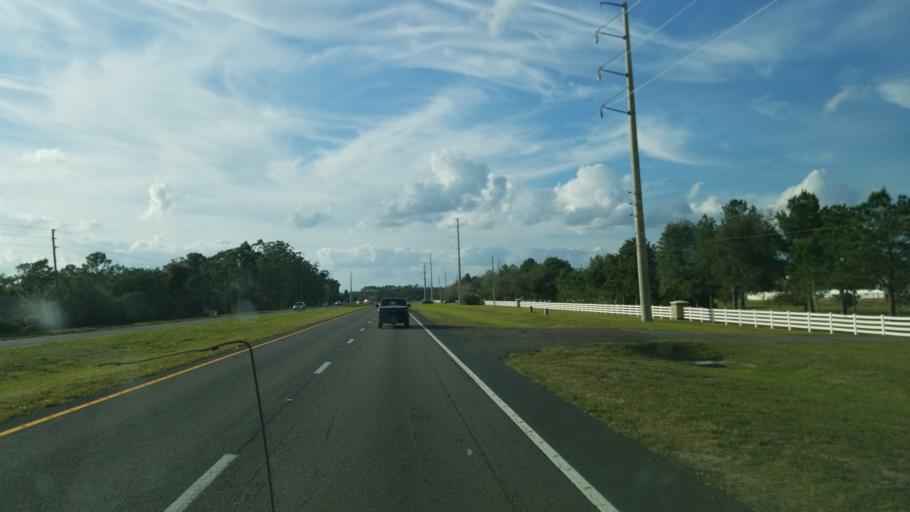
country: US
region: Florida
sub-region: Osceola County
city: Saint Cloud
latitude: 28.1933
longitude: -81.1573
